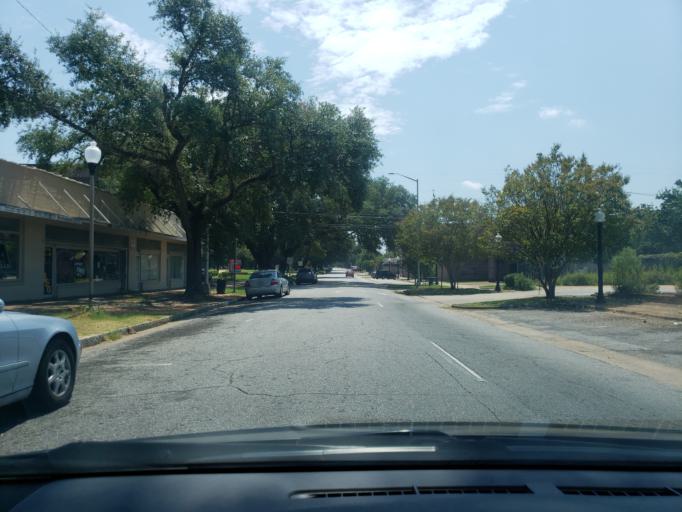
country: US
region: Georgia
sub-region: Dougherty County
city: Albany
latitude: 31.5750
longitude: -84.1536
